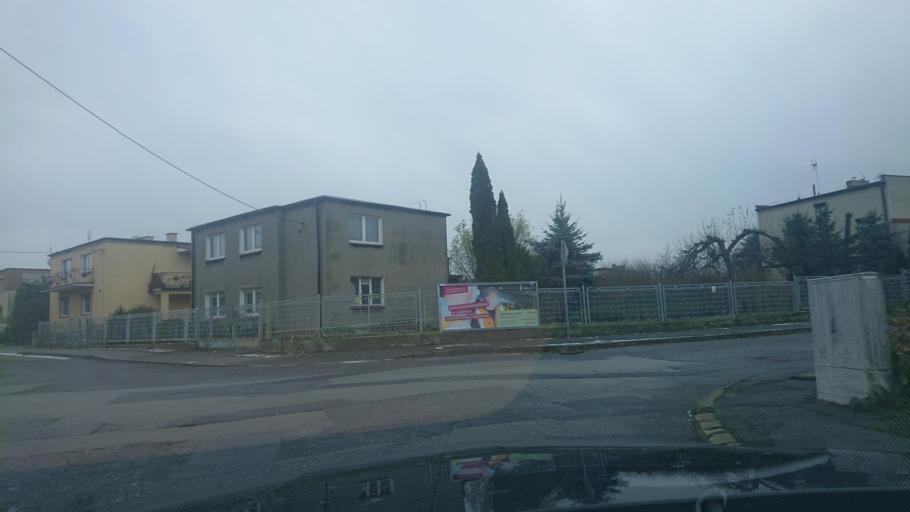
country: PL
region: Greater Poland Voivodeship
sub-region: Powiat gnieznienski
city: Gniezno
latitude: 52.5395
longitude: 17.5749
